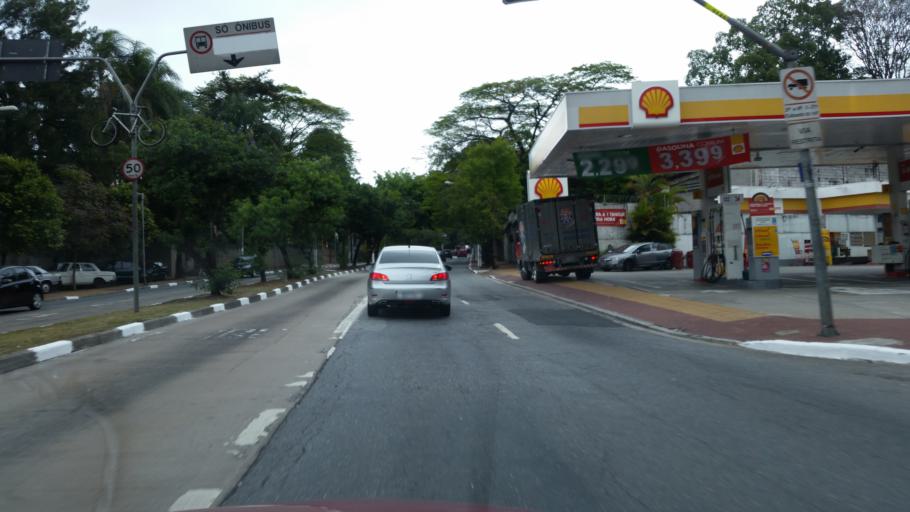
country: BR
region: Sao Paulo
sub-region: Diadema
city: Diadema
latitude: -23.6296
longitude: -46.6868
